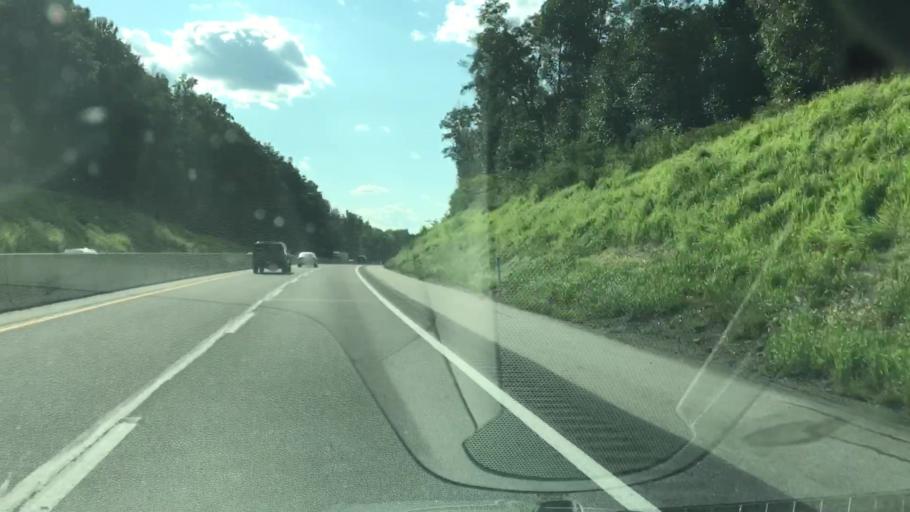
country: US
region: Pennsylvania
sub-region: Lebanon County
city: Cornwall
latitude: 40.2265
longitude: -76.4780
